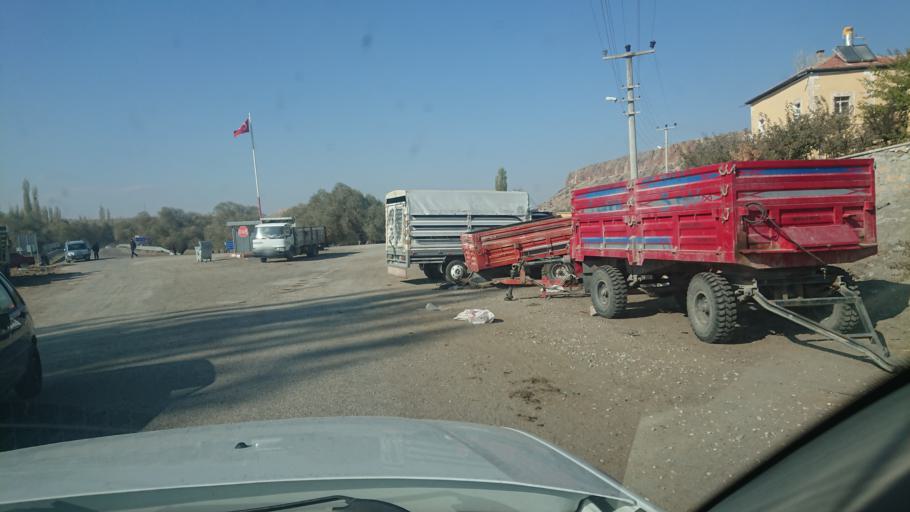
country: TR
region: Aksaray
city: Gulagac
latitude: 38.3544
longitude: 34.2316
